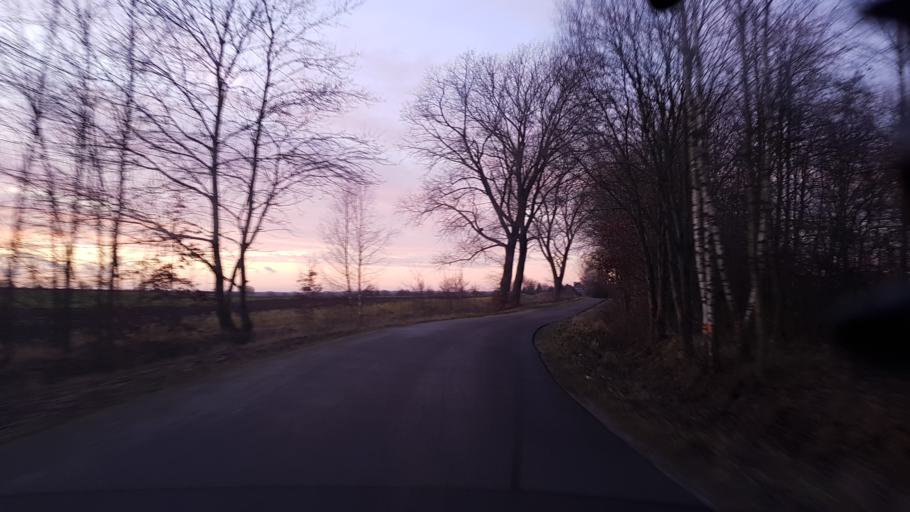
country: PL
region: Pomeranian Voivodeship
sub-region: Powiat bytowski
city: Tuchomie
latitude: 54.1281
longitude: 17.3724
